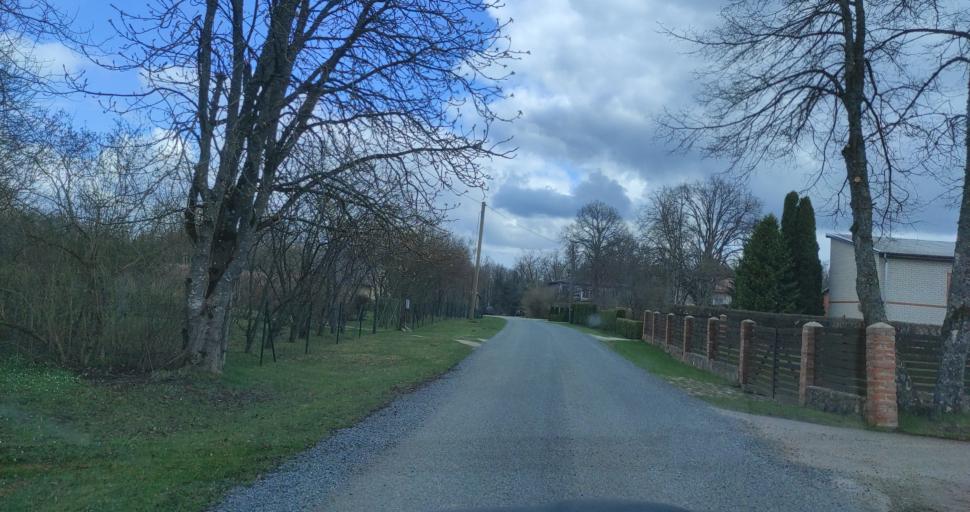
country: LV
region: Aizpute
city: Aizpute
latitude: 56.7115
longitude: 21.5682
